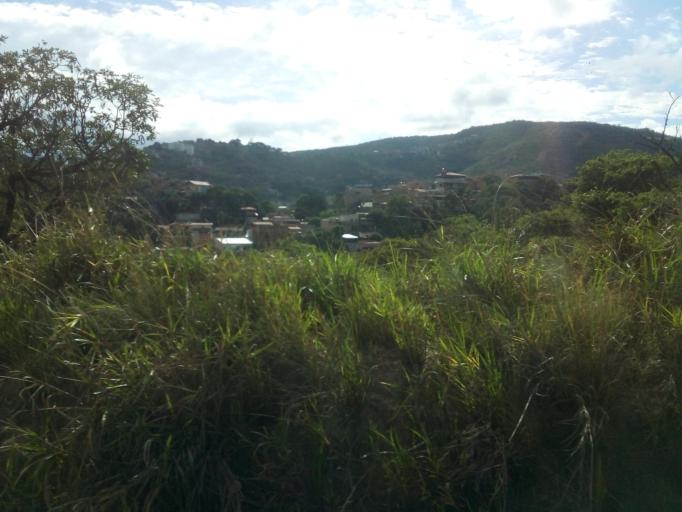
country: BR
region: Minas Gerais
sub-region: Belo Horizonte
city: Belo Horizonte
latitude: -19.8899
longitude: -43.8634
